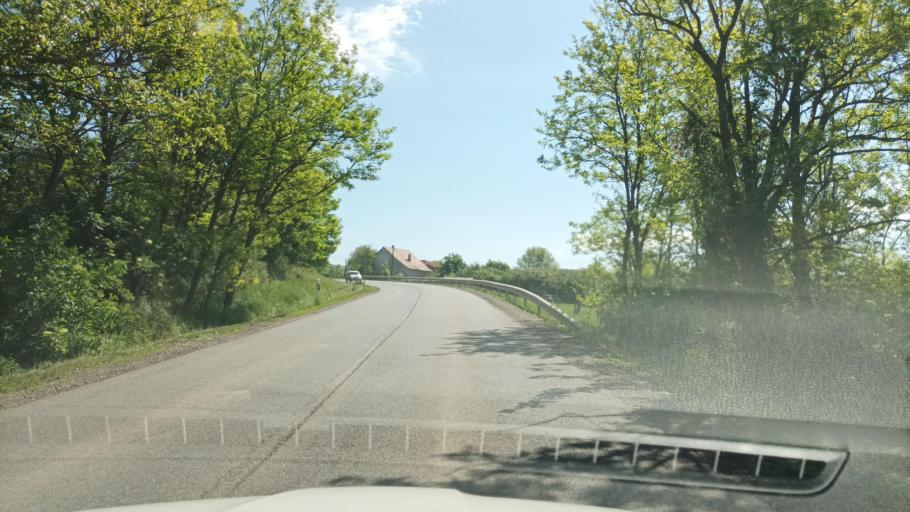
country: HU
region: Pest
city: Kosd
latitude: 47.7972
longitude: 19.2443
